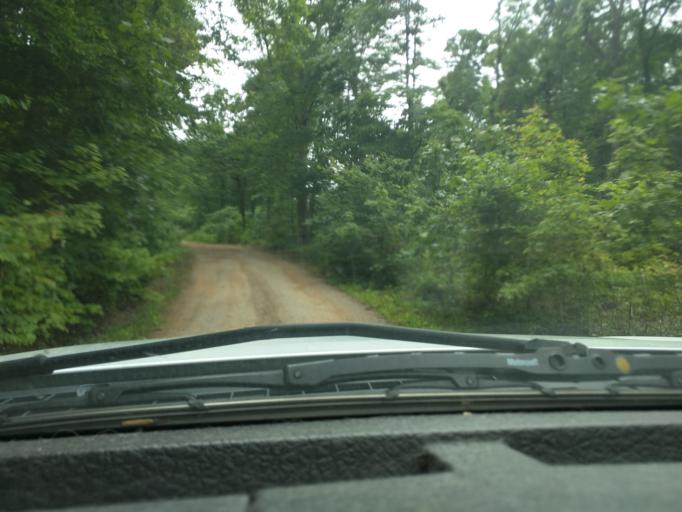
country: US
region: Arkansas
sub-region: Madison County
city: Huntsville
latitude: 35.8696
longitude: -93.5282
